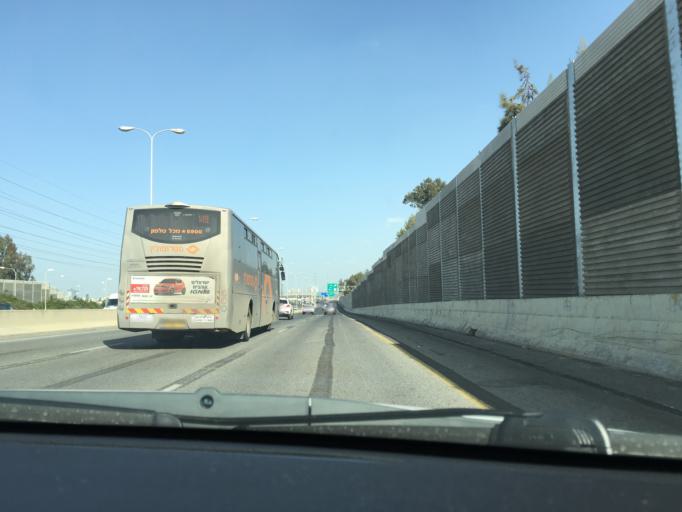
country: IL
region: Central District
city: Hod HaSharon
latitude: 32.1659
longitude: 34.8805
